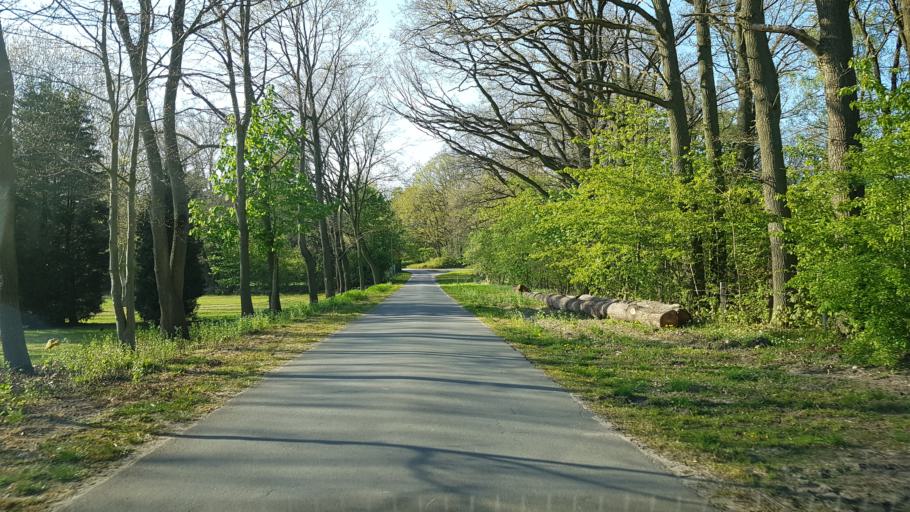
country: DE
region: Lower Saxony
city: Altenmedingen
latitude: 53.1723
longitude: 10.6125
